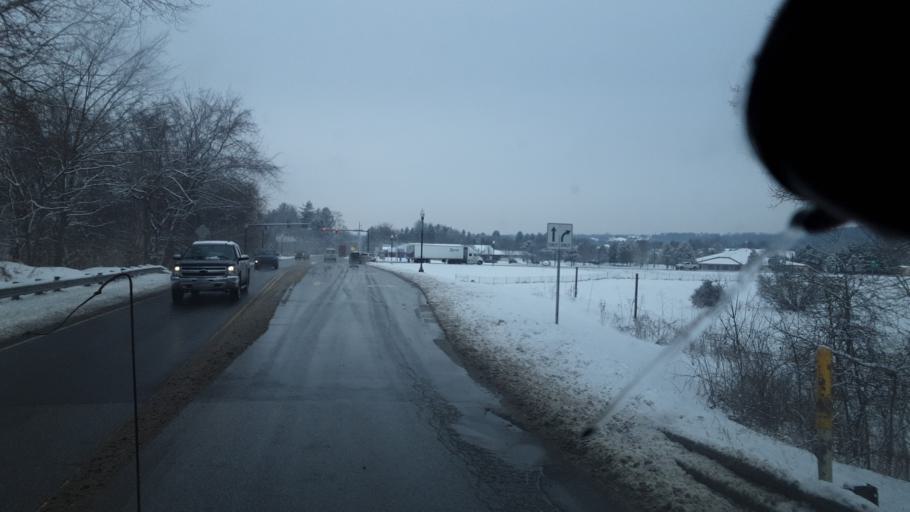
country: US
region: Ohio
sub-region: Licking County
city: Heath
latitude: 40.0481
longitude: -82.4750
